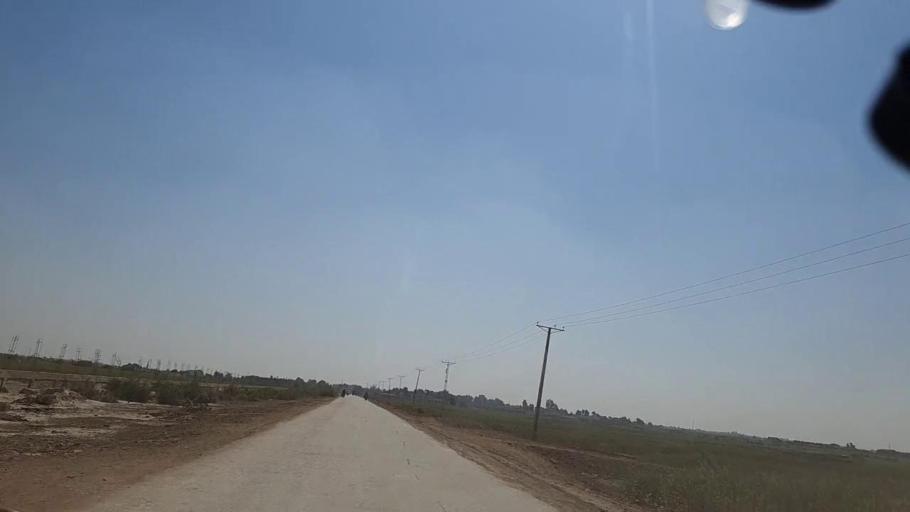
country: PK
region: Sindh
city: Mirpur Khas
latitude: 25.4937
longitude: 69.0384
